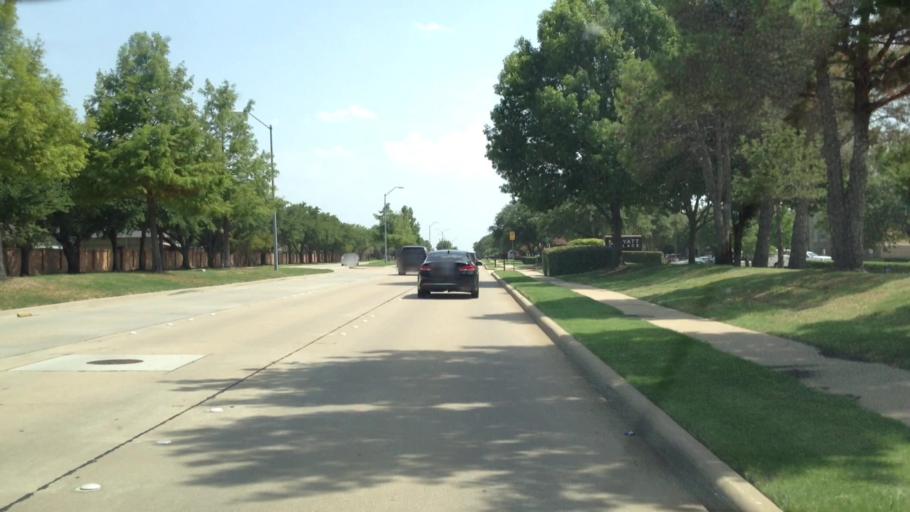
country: US
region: Texas
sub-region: Denton County
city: The Colony
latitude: 33.0422
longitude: -96.8275
